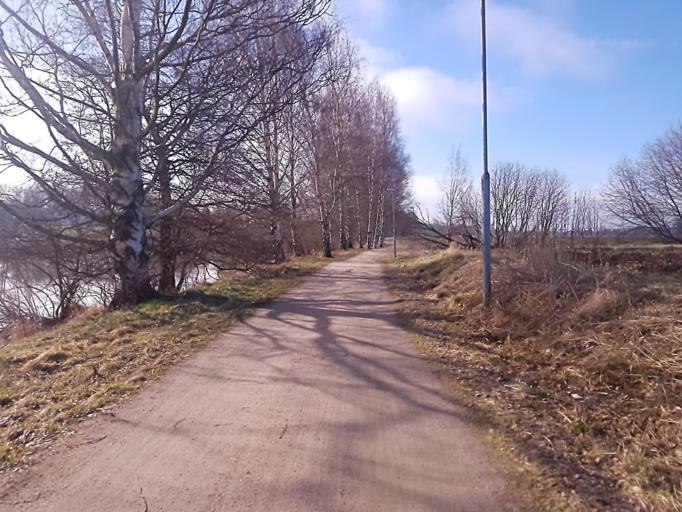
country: FI
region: Uusimaa
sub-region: Helsinki
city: Vantaa
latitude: 60.2613
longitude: 24.9736
